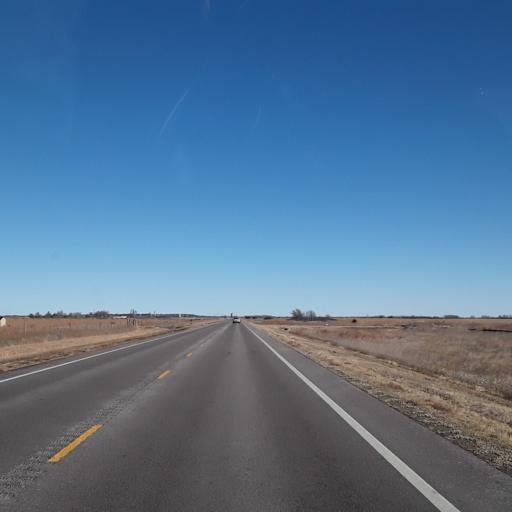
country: US
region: Kansas
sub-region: Pawnee County
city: Larned
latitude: 38.1350
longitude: -99.1576
